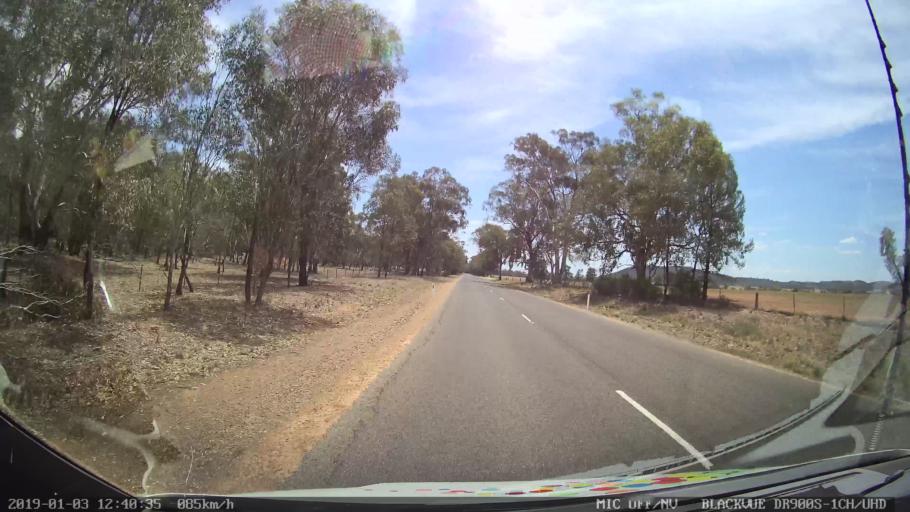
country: AU
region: New South Wales
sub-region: Weddin
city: Grenfell
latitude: -33.8108
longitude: 148.2130
